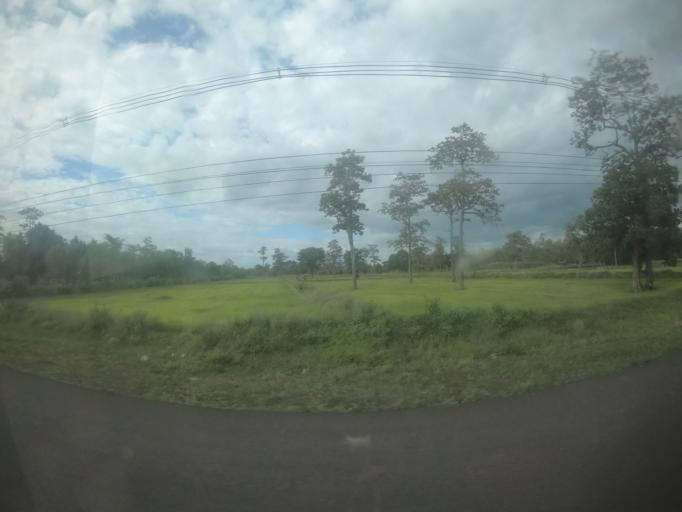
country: TH
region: Surin
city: Prasat
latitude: 14.5726
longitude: 103.4859
